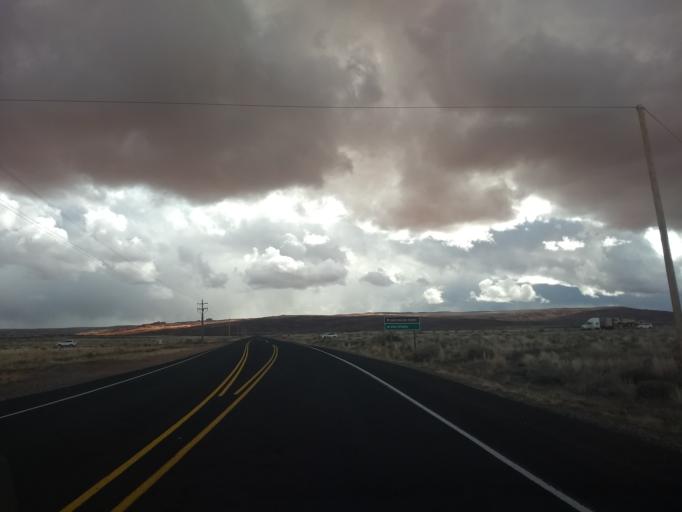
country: US
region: Utah
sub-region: Washington County
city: Hurricane
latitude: 37.1339
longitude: -113.3927
